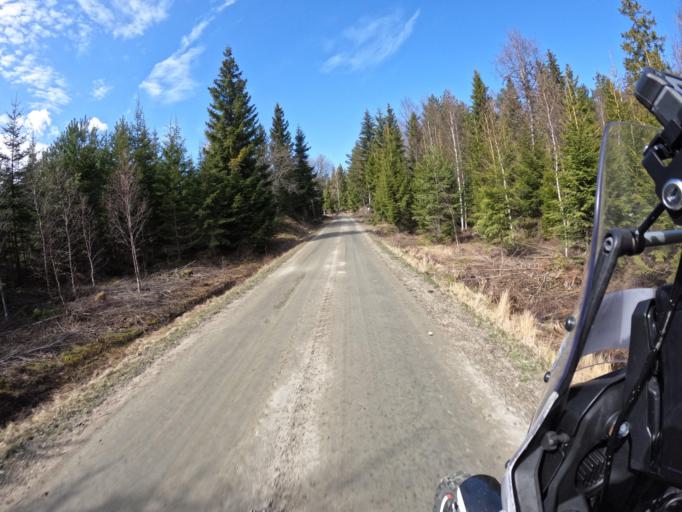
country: SE
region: Vaestra Goetaland
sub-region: Ulricehamns Kommun
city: Ulricehamn
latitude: 57.9326
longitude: 13.6071
